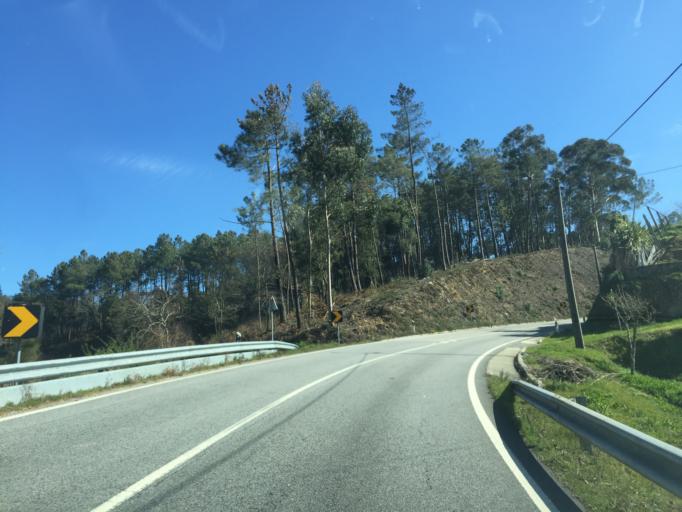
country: PT
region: Aveiro
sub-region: Vale de Cambra
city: Macieira de Cambra
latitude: 40.8905
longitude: -8.3585
